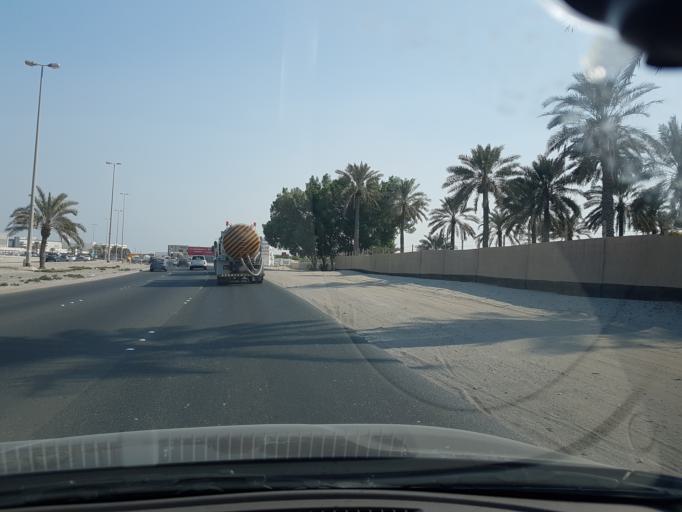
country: BH
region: Northern
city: Sitrah
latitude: 26.1612
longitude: 50.6047
